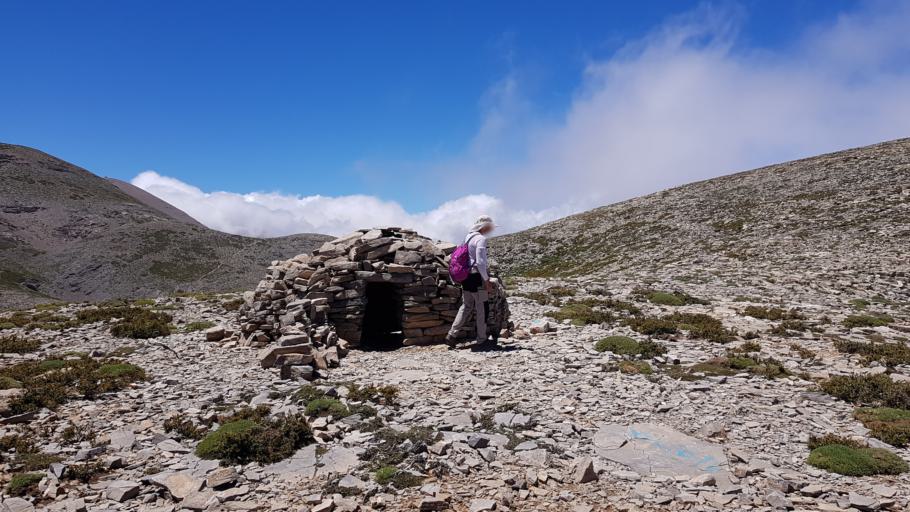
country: GR
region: Crete
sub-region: Nomos Rethymnis
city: Zoniana
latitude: 35.2202
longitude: 24.7976
